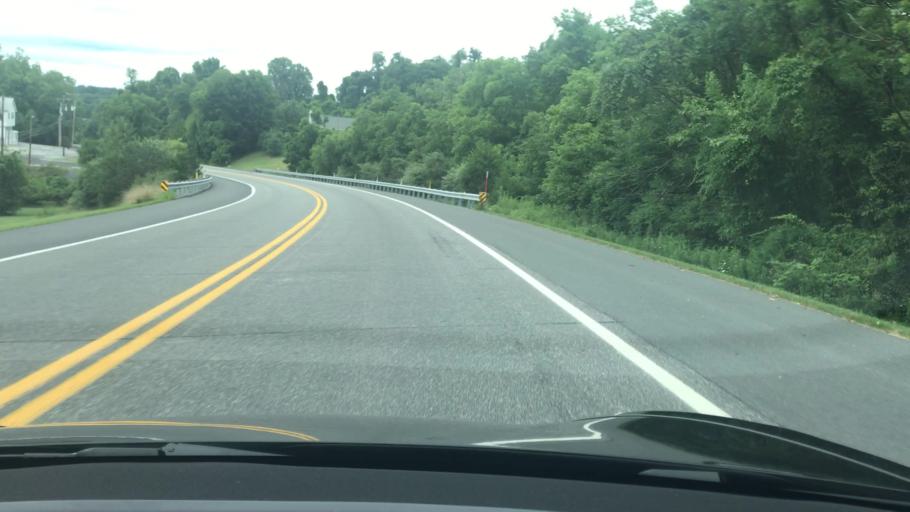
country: US
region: Pennsylvania
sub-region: Cumberland County
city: Lower Allen
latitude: 40.1644
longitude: -76.8851
